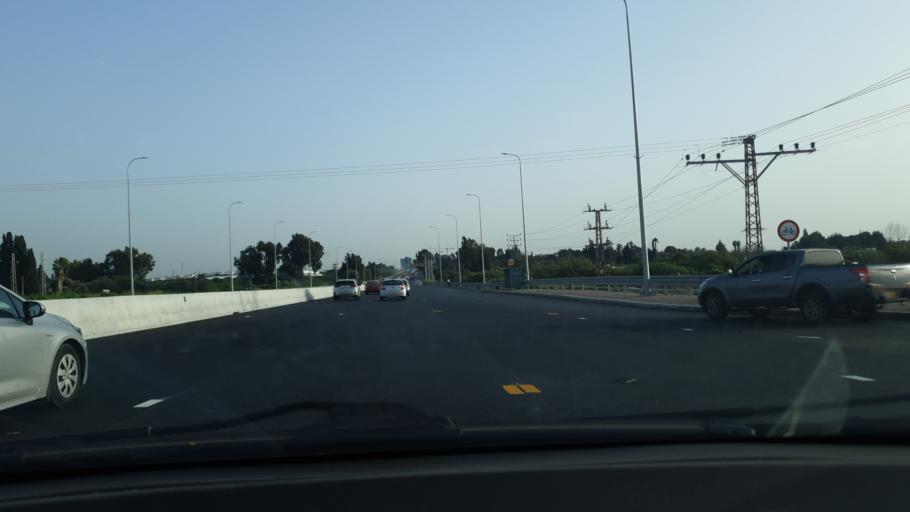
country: IL
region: Central District
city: Ra'anana
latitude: 32.2189
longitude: 34.8832
